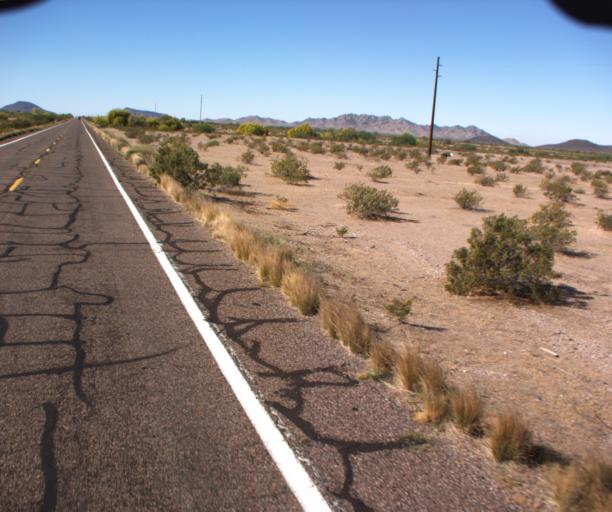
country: US
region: Arizona
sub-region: Maricopa County
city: Gila Bend
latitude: 32.8428
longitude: -112.7756
